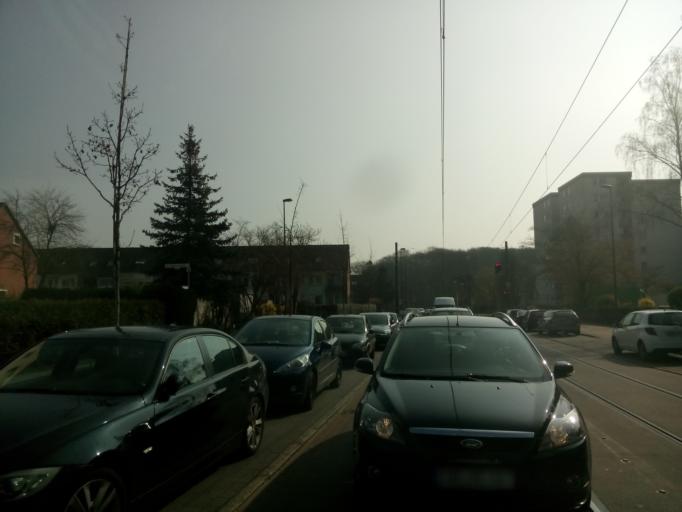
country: DE
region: Lower Saxony
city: Oyten
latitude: 53.0664
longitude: 8.9543
